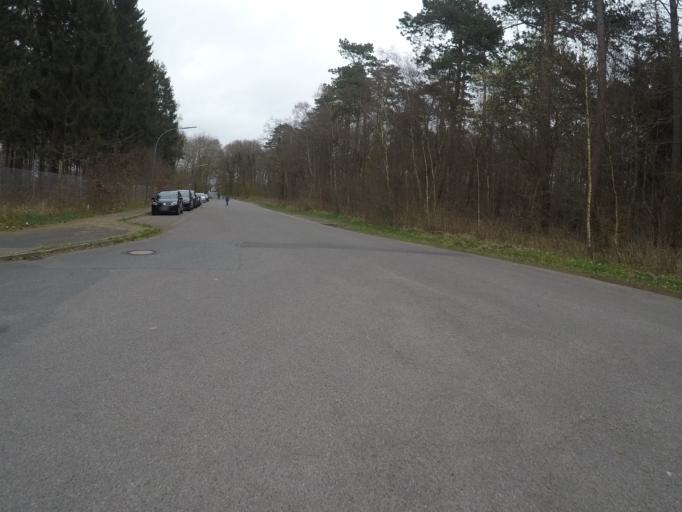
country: DE
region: Lower Saxony
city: Nordholz
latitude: 53.8072
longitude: 8.6558
